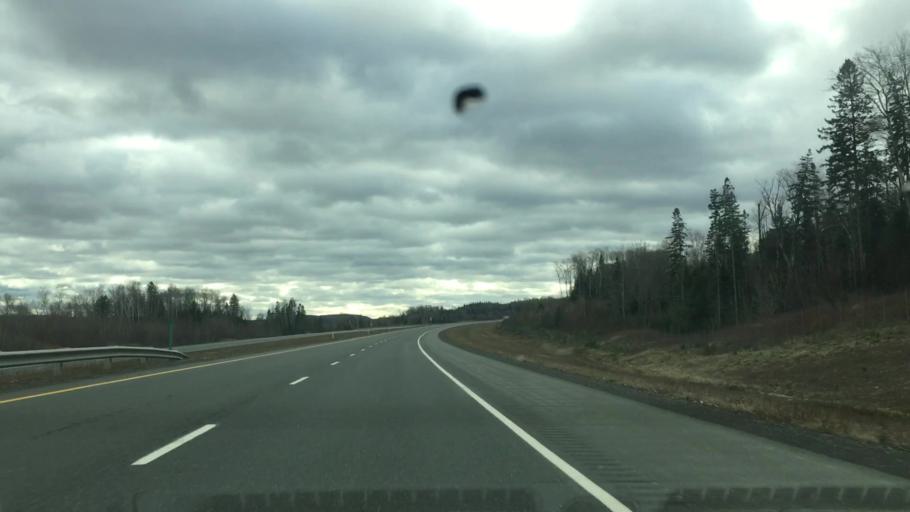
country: US
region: Maine
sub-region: Aroostook County
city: Fort Fairfield
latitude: 46.6757
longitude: -67.7297
